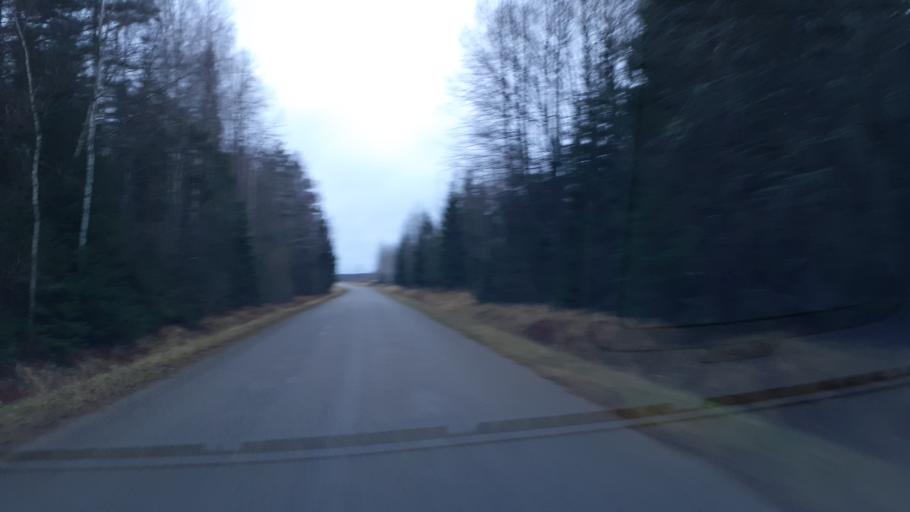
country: LV
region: Kuldigas Rajons
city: Kuldiga
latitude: 57.0353
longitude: 22.1550
